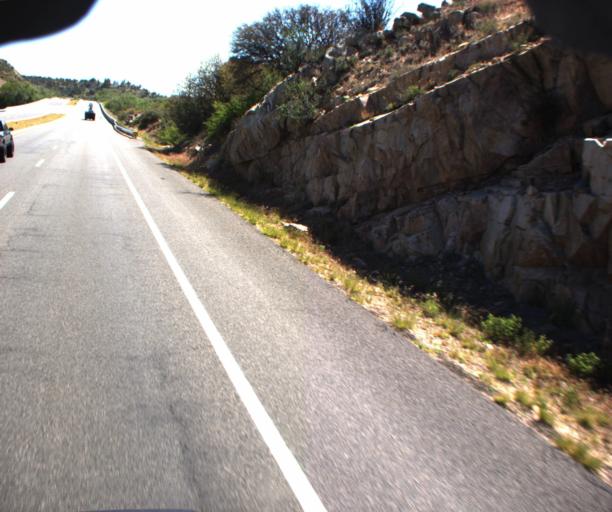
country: US
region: Arizona
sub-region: Yavapai County
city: Prescott
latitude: 34.5603
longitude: -112.4462
